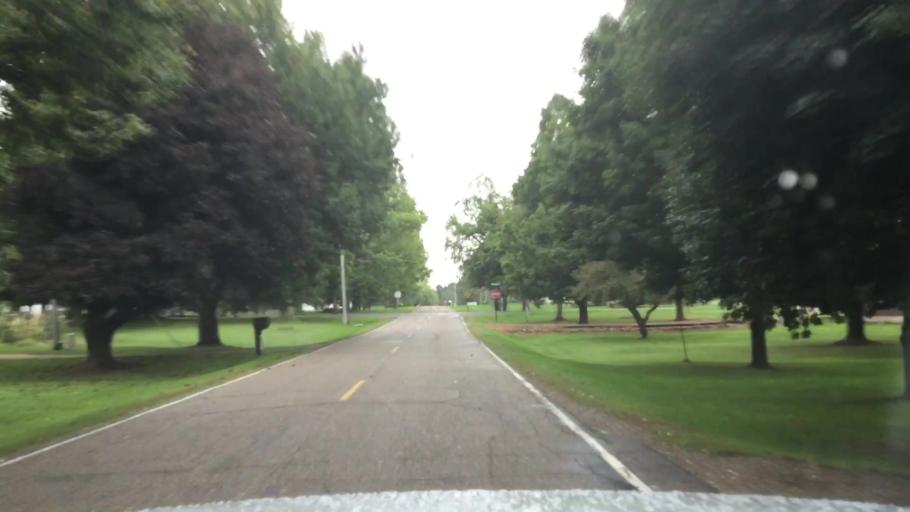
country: US
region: Michigan
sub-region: Shiawassee County
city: Perry
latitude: 42.8938
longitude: -84.2022
